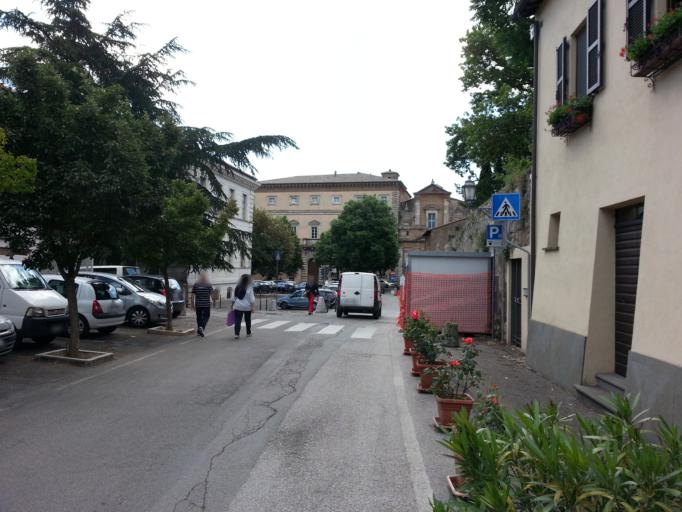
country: IT
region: Umbria
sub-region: Provincia di Terni
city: Orvieto
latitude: 42.7176
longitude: 12.1143
